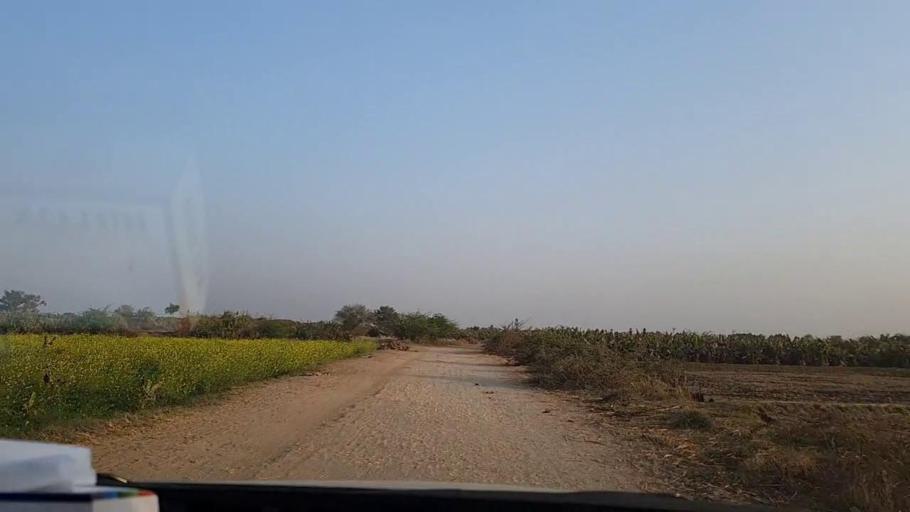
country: PK
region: Sindh
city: Tando Ghulam Ali
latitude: 25.1858
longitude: 68.9132
